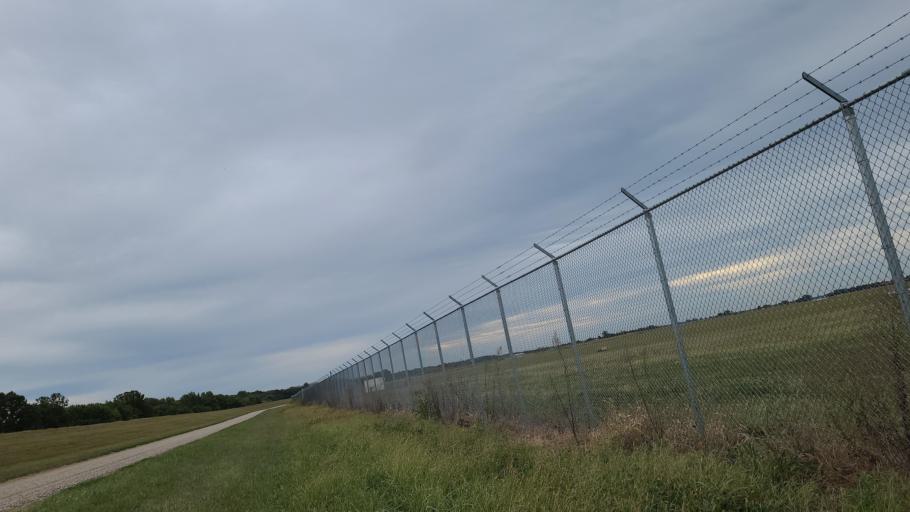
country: US
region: Kansas
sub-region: Douglas County
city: Lawrence
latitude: 39.0223
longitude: -95.2223
